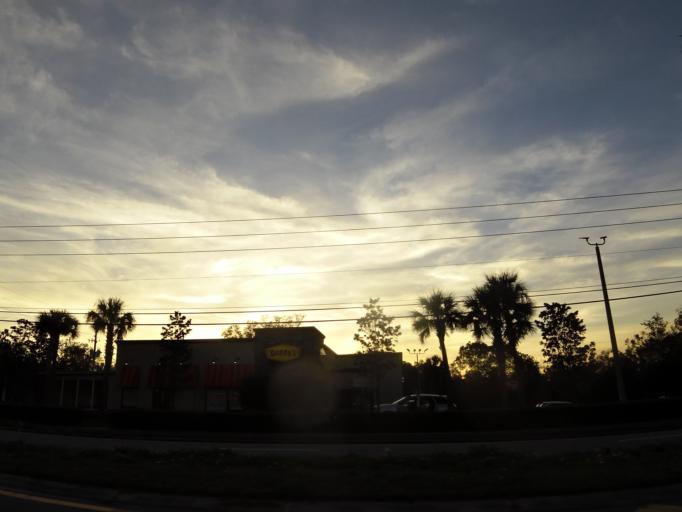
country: US
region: Florida
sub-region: Volusia County
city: North DeLand
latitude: 29.0491
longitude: -81.3041
